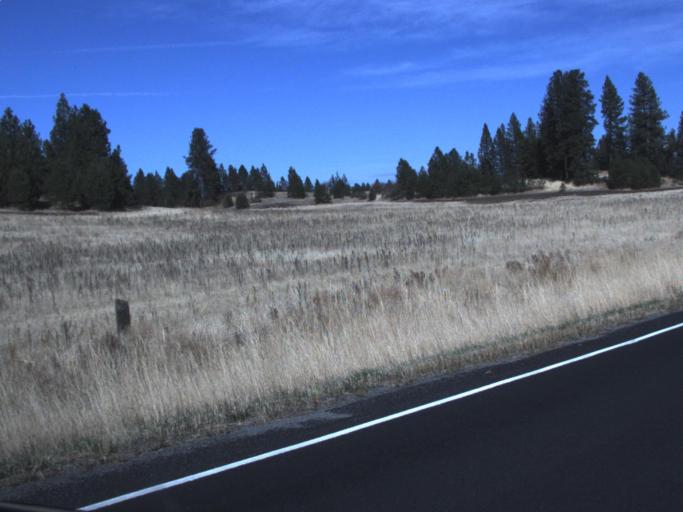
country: US
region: Washington
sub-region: Lincoln County
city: Davenport
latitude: 48.0101
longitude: -118.2547
